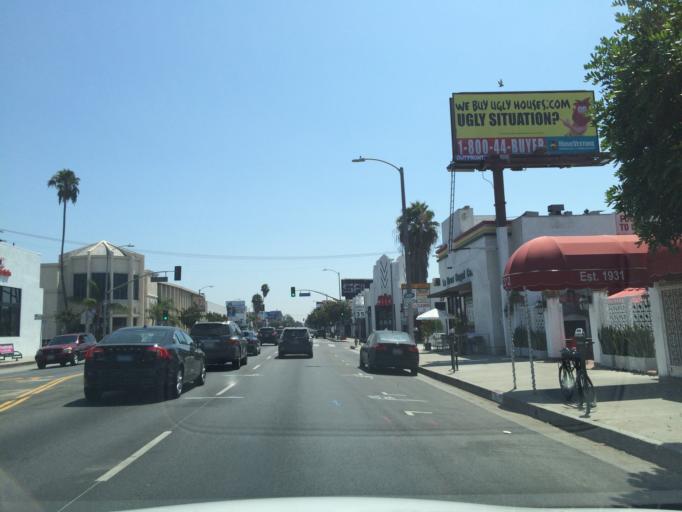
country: US
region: California
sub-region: Los Angeles County
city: West Hollywood
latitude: 34.0761
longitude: -118.3494
